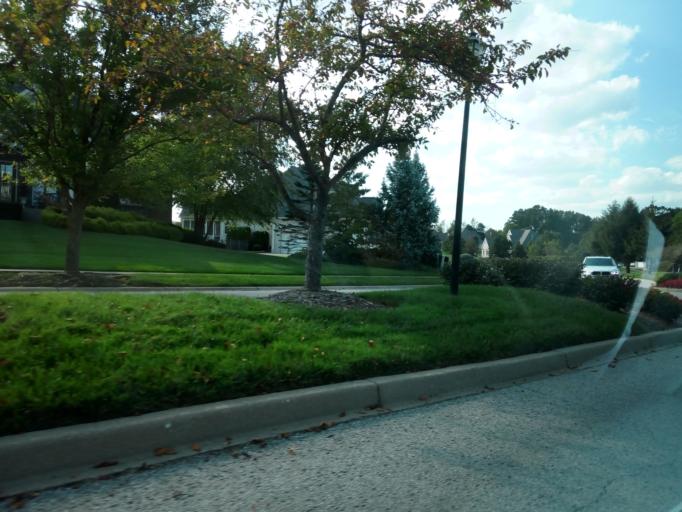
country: US
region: Kentucky
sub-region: Oldham County
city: Pewee Valley
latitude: 38.2723
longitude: -85.4805
